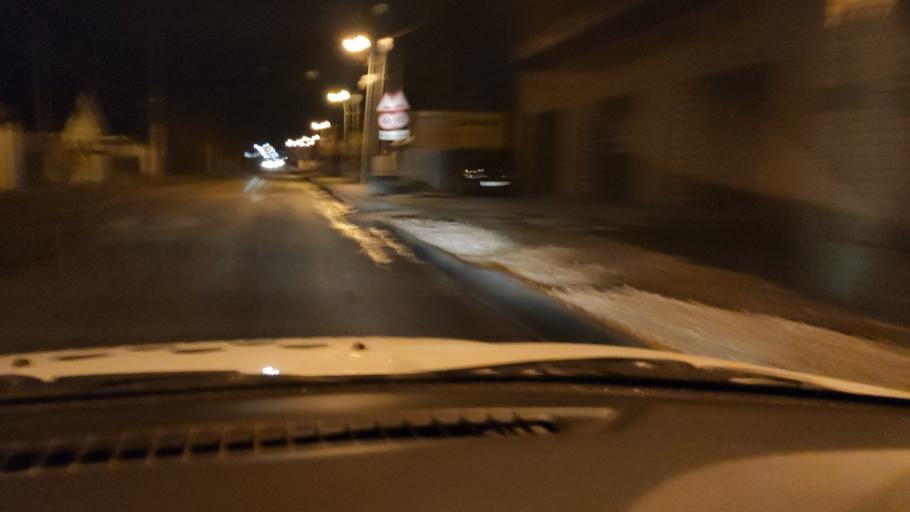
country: RU
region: Perm
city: Kondratovo
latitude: 57.9651
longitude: 56.1203
